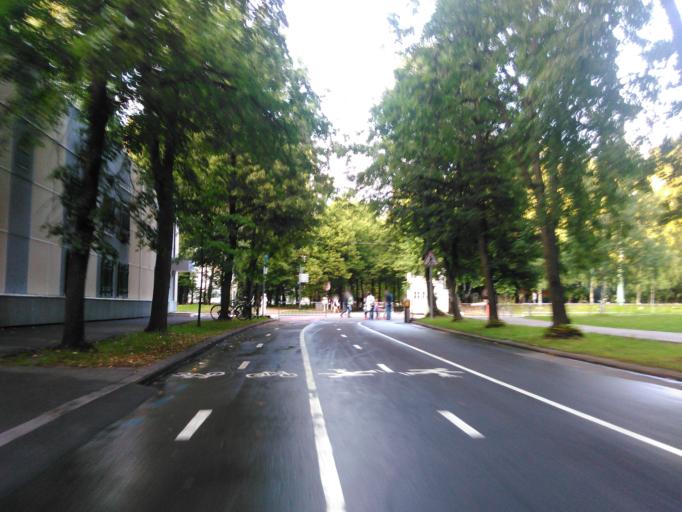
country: RU
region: Moscow
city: Sokol'niki
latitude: 55.7984
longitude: 37.6701
